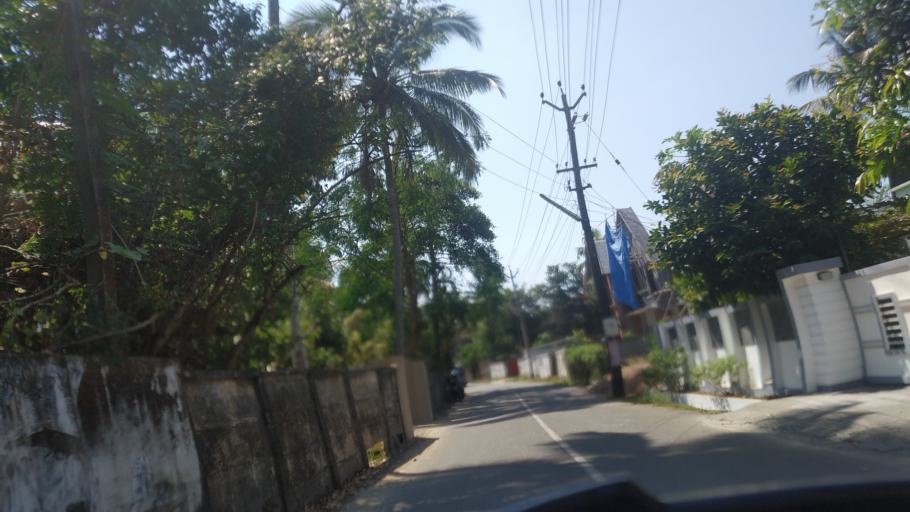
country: IN
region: Kerala
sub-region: Ernakulam
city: Elur
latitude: 10.1313
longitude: 76.2341
